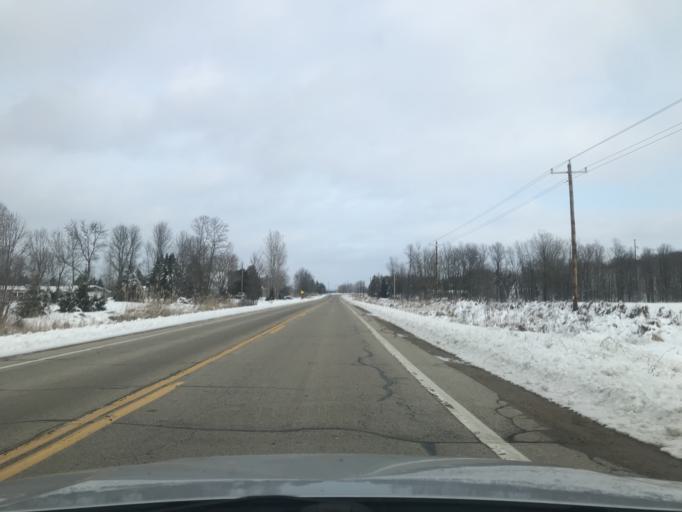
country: US
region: Wisconsin
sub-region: Oconto County
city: Oconto Falls
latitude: 44.8901
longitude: -88.0049
